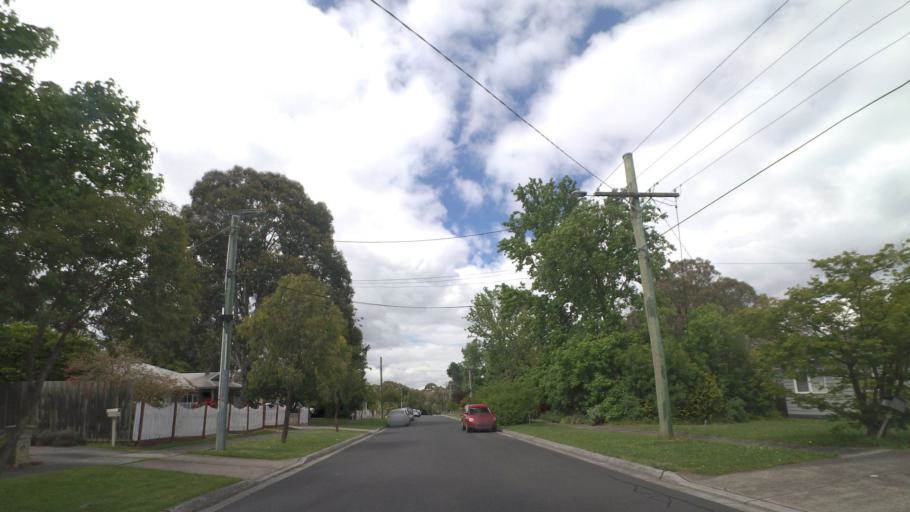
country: AU
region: Victoria
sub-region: Maroondah
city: Croydon North
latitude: -37.7838
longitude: 145.2904
